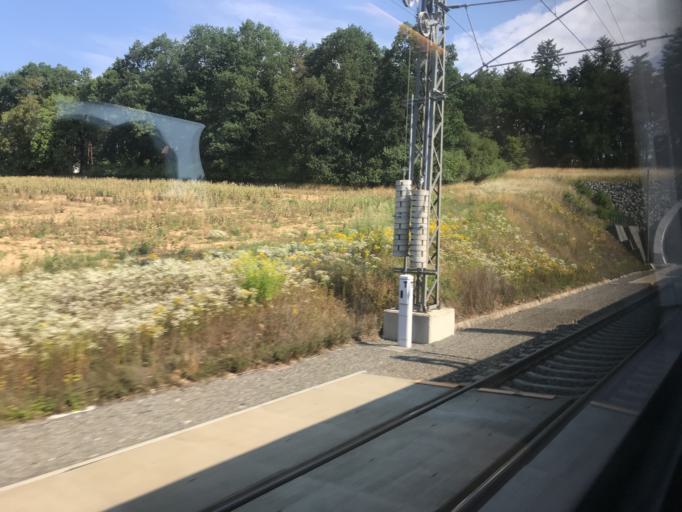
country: CZ
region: Central Bohemia
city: Bystrice
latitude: 49.7029
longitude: 14.6607
